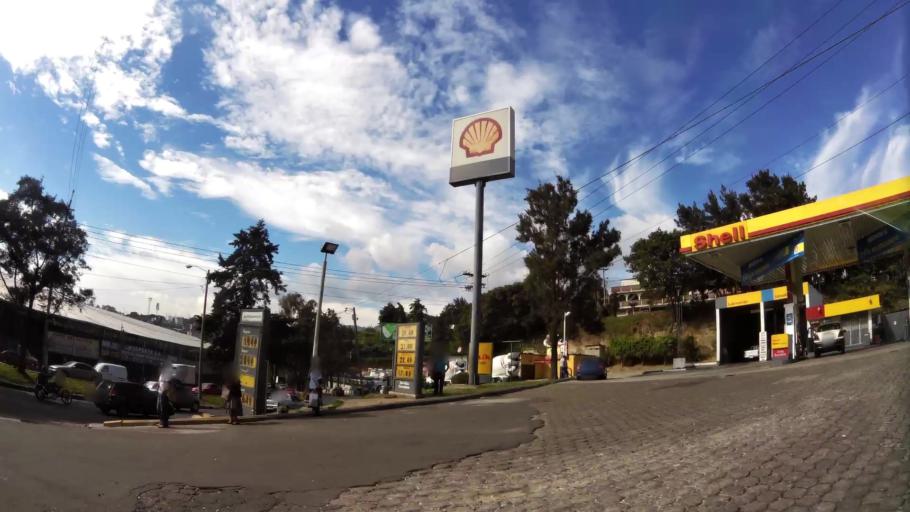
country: GT
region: Guatemala
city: Mixco
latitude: 14.6353
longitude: -90.5985
